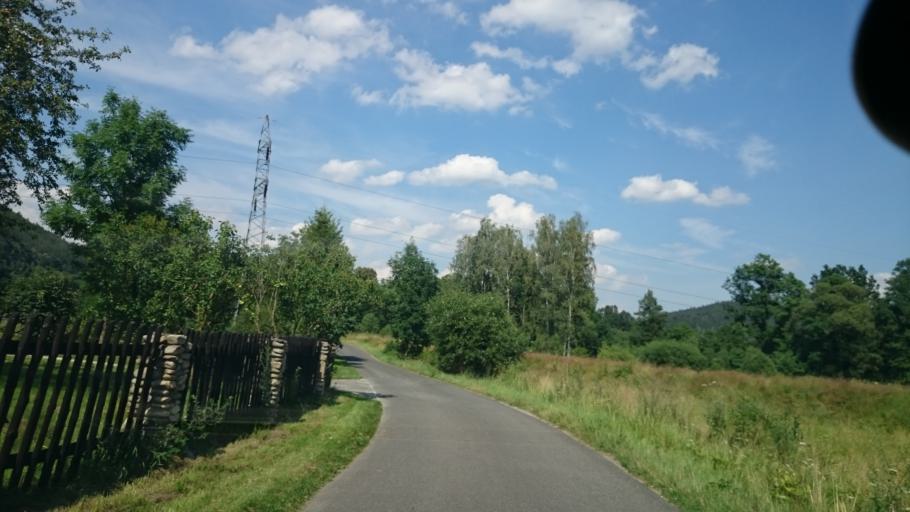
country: PL
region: Lower Silesian Voivodeship
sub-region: Powiat klodzki
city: Ladek-Zdroj
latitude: 50.3451
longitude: 16.8224
